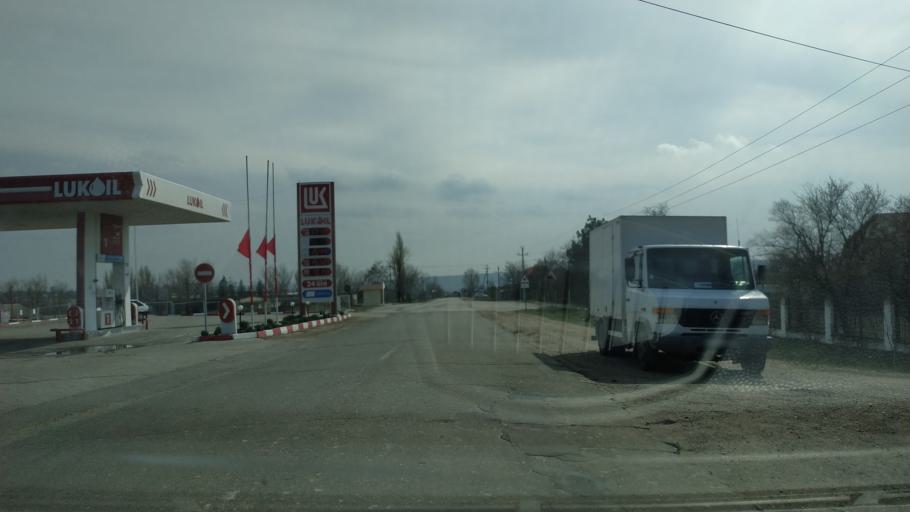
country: MD
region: Gagauzia
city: Vulcanesti
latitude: 45.6986
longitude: 28.4031
